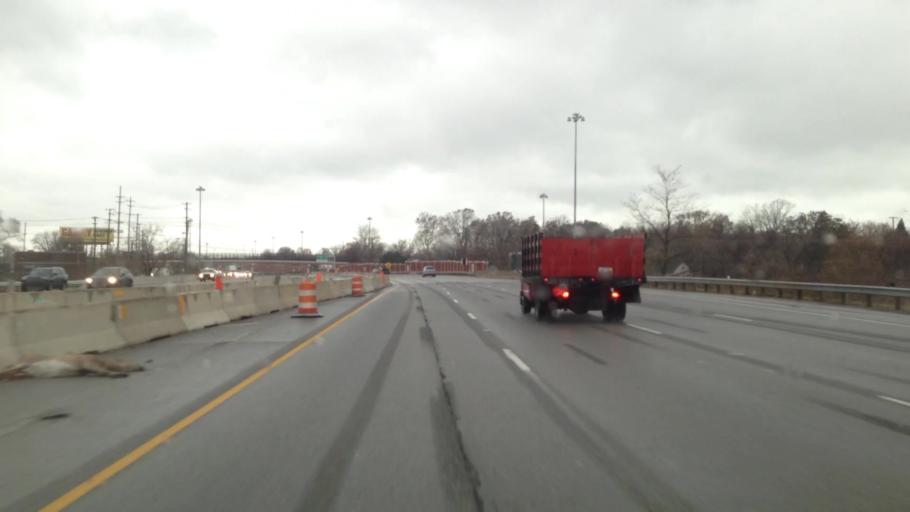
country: US
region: Ohio
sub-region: Cuyahoga County
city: Euclid
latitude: 41.5782
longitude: -81.5485
